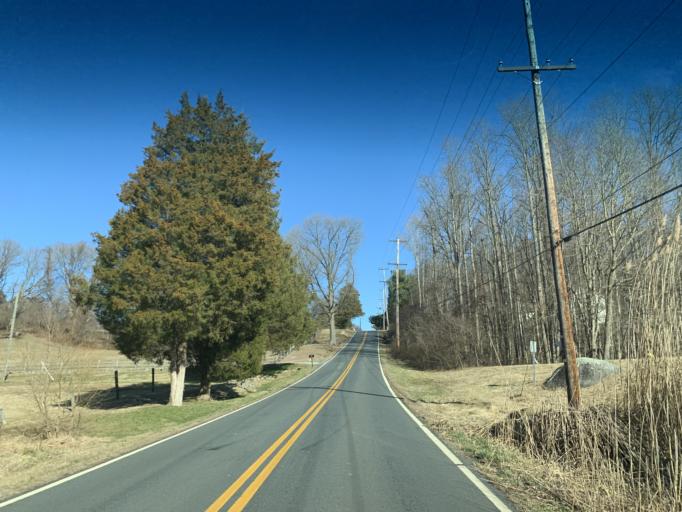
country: US
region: Maryland
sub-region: Cecil County
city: Rising Sun
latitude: 39.6704
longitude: -76.1209
